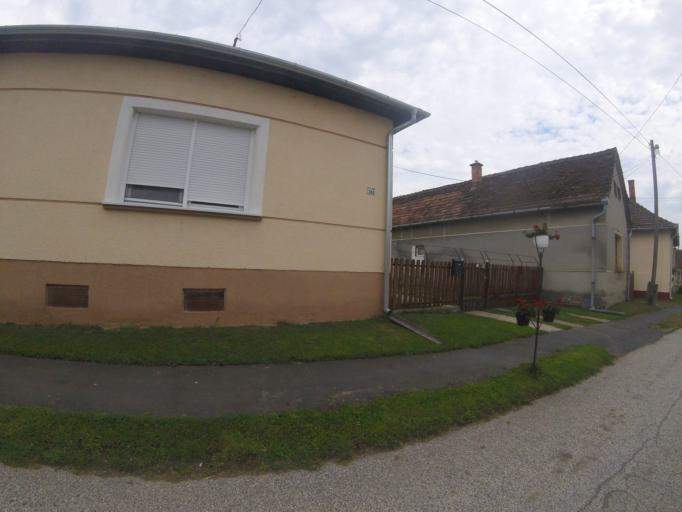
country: HR
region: Medimurska
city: Podturen
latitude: 46.5378
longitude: 16.5915
